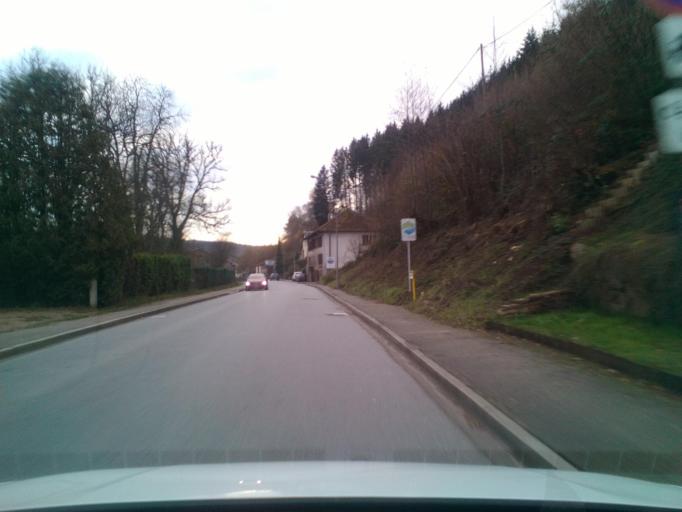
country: FR
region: Lorraine
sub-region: Departement des Vosges
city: Senones
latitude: 48.4029
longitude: 6.9871
